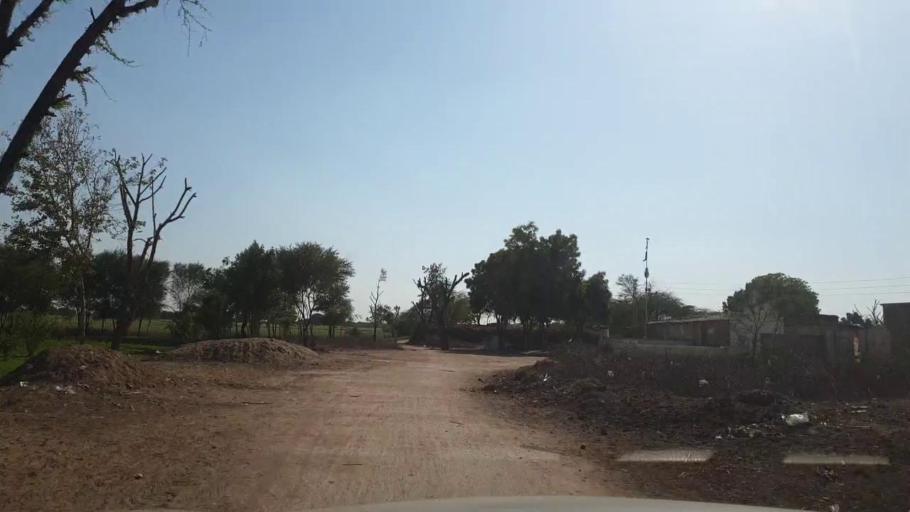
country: PK
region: Sindh
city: Tando Adam
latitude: 25.6610
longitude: 68.6936
